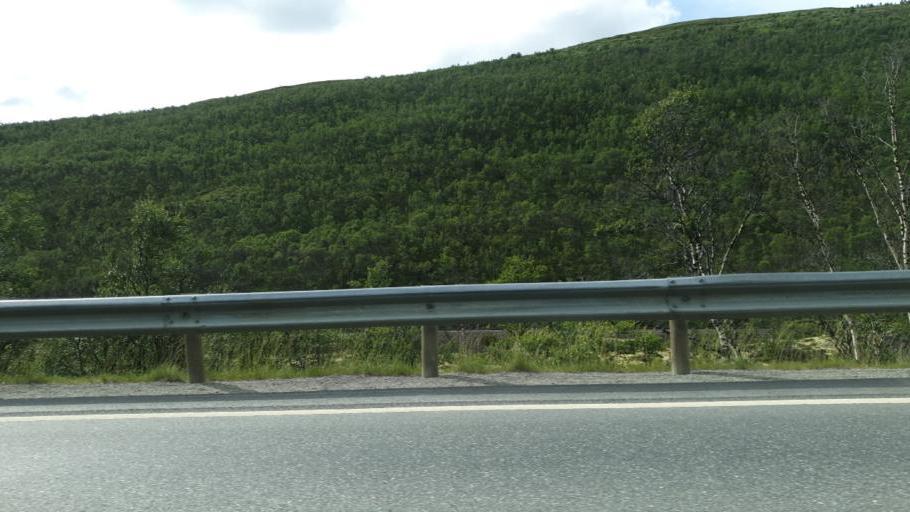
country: NO
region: Sor-Trondelag
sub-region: Oppdal
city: Oppdal
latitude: 62.3110
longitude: 9.6125
